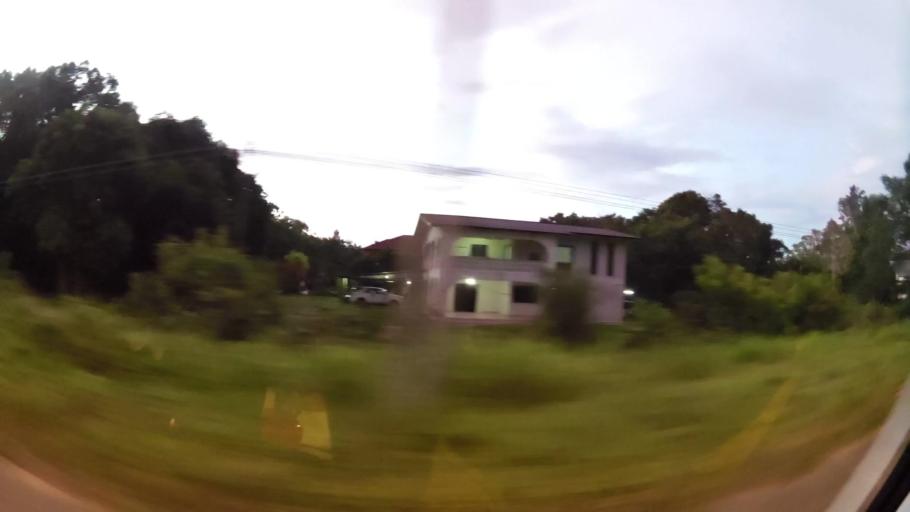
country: BN
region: Belait
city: Seria
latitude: 4.6469
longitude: 114.4099
